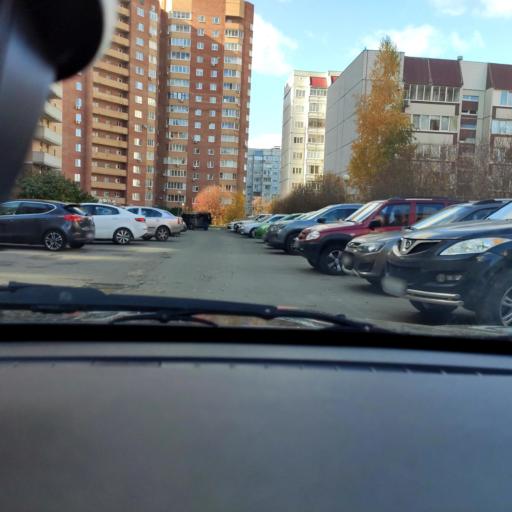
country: RU
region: Samara
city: Tol'yatti
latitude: 53.5002
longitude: 49.2854
